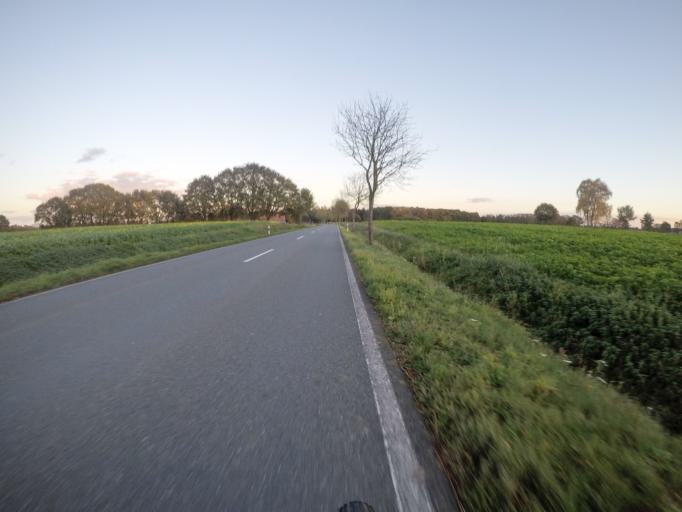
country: DE
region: North Rhine-Westphalia
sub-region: Regierungsbezirk Munster
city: Isselburg
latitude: 51.8441
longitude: 6.4840
